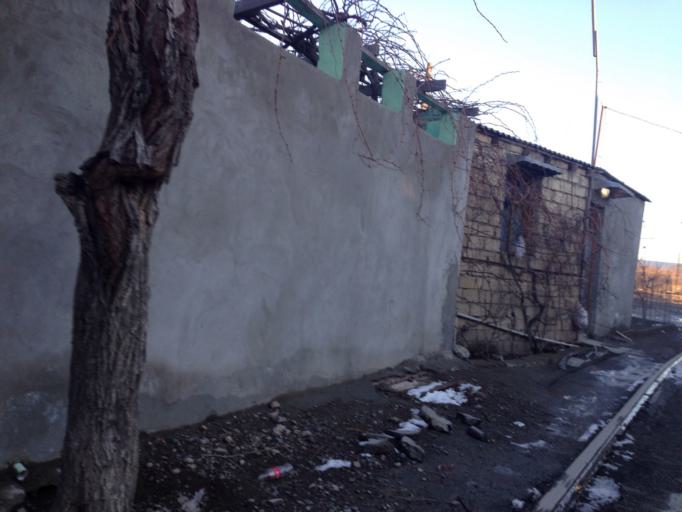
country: AZ
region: Baki
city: Baku
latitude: 40.4220
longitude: 49.8660
